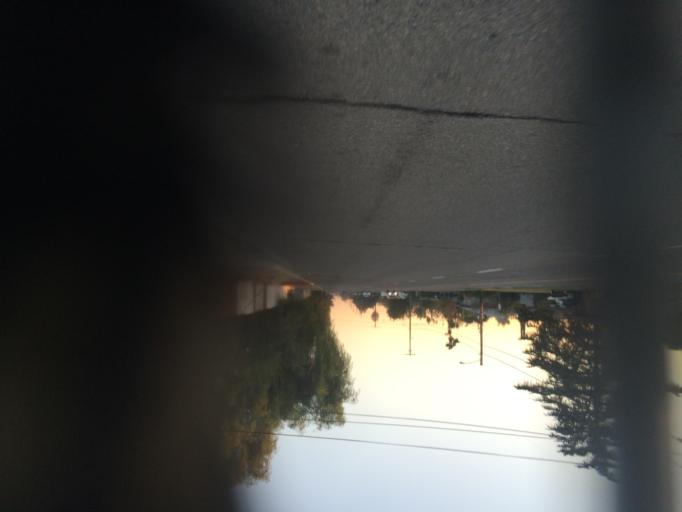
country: US
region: California
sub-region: Fresno County
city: Fresno
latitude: 36.7776
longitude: -119.7454
